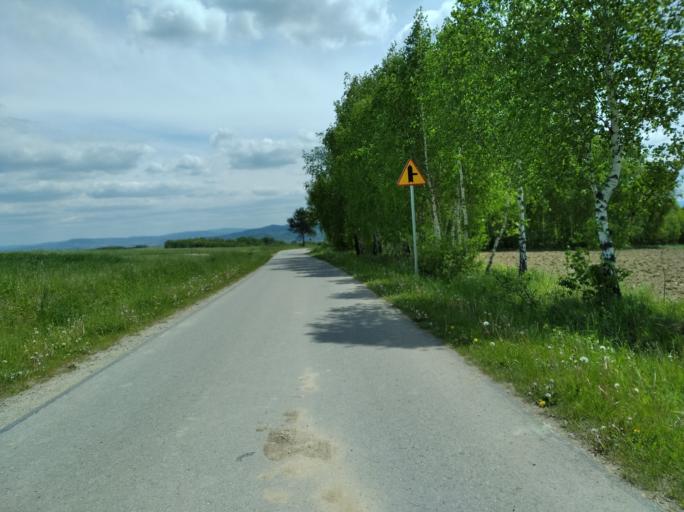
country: PL
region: Subcarpathian Voivodeship
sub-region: Powiat ropczycko-sedziszowski
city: Wielopole Skrzynskie
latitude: 49.8989
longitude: 21.6103
